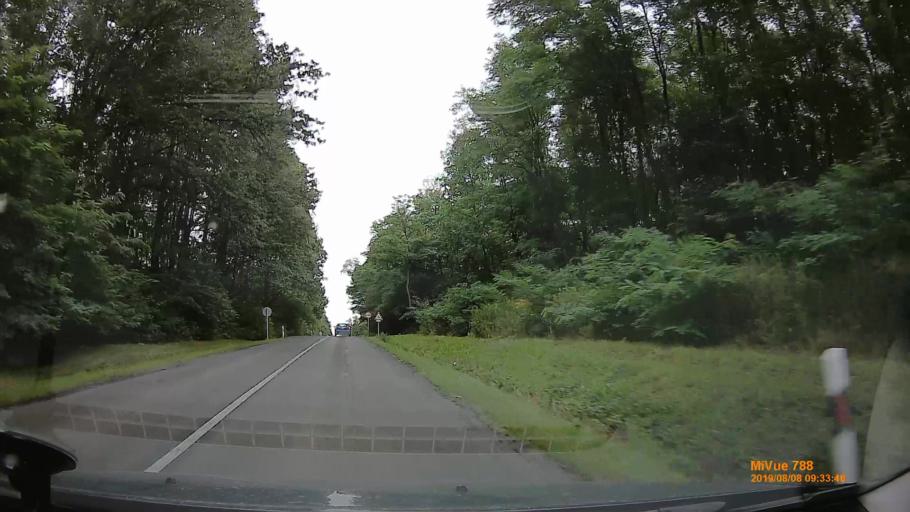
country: HU
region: Vas
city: Vasvar
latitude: 47.0260
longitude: 16.8171
